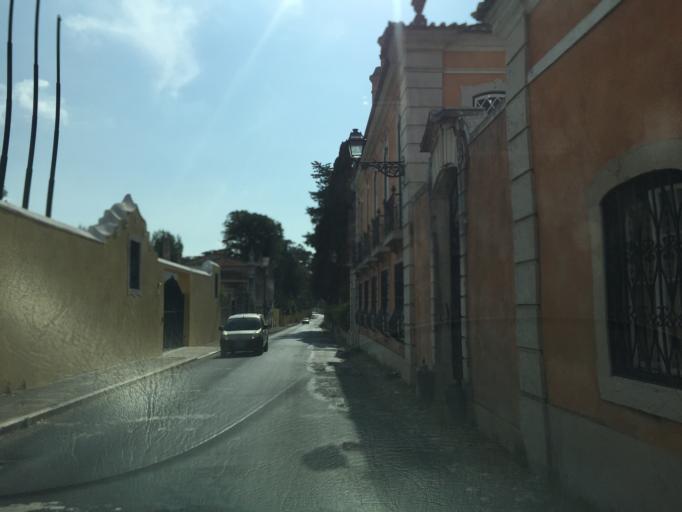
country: PT
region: Lisbon
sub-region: Odivelas
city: Olival do Basto
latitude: 38.7718
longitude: -9.1744
